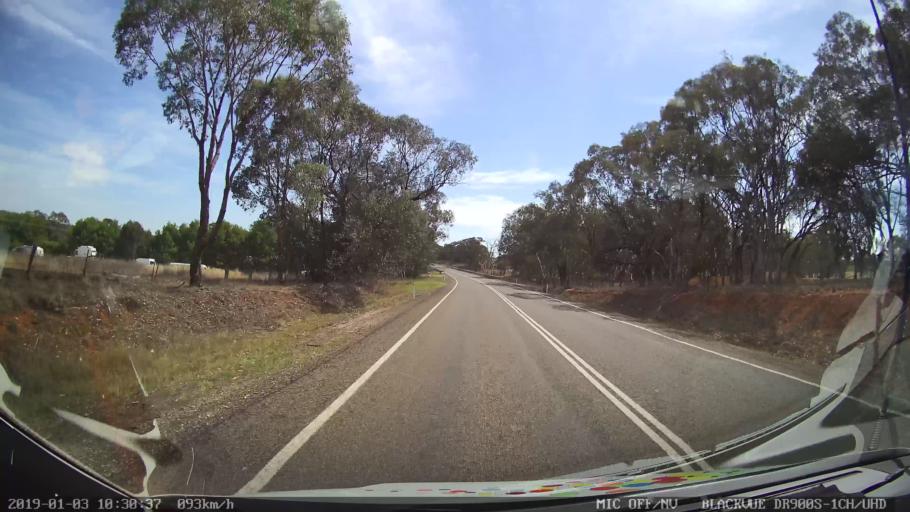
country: AU
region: New South Wales
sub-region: Young
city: Young
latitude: -34.3602
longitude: 148.2703
